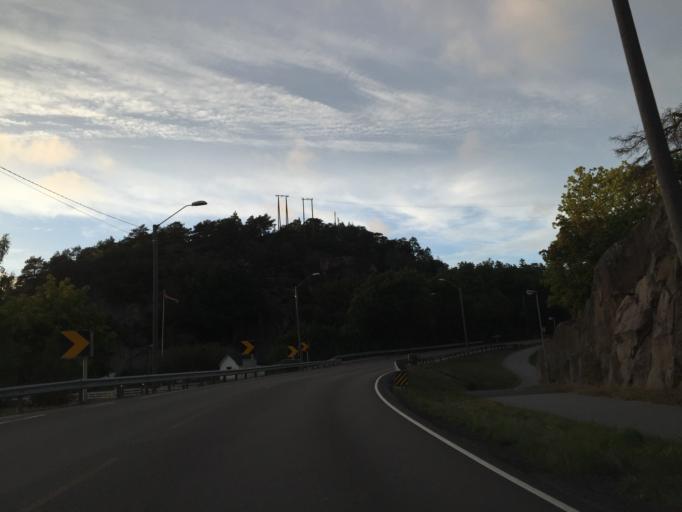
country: NO
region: Ostfold
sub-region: Fredrikstad
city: Fredrikstad
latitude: 59.1818
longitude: 10.9260
